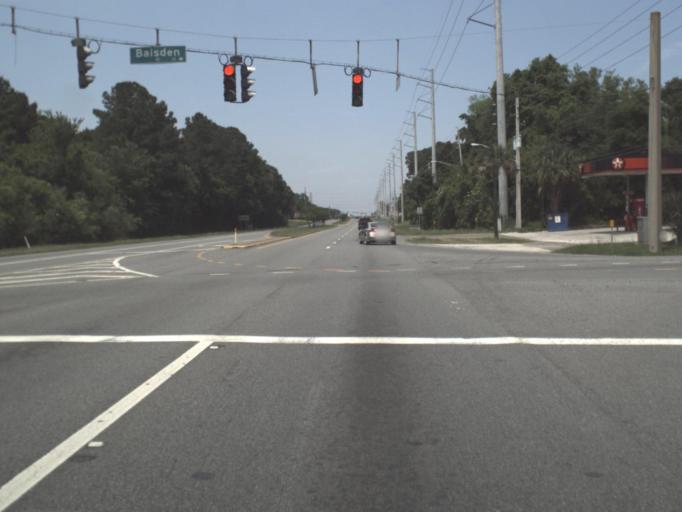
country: US
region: Florida
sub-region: Duval County
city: Jacksonville
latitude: 30.4411
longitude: -81.6412
